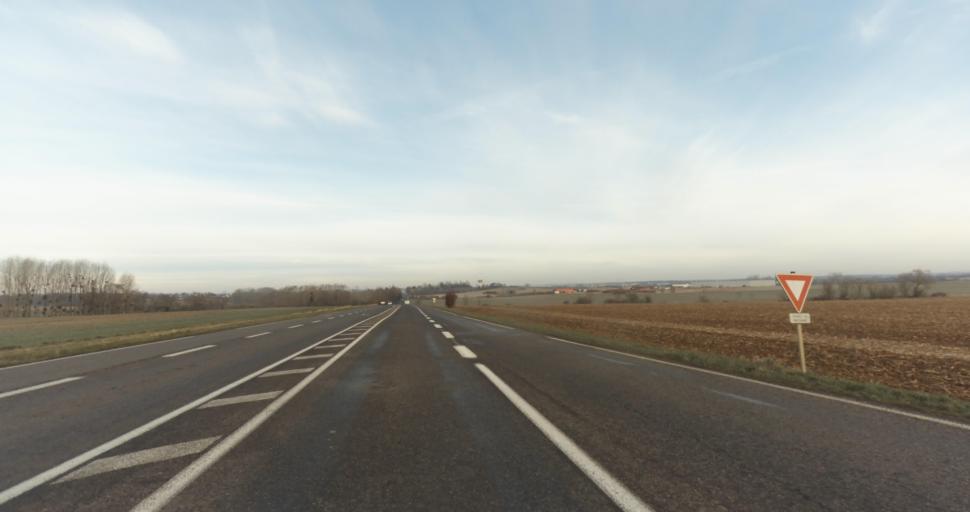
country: FR
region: Lorraine
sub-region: Departement de Meurthe-et-Moselle
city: Doncourt-les-Conflans
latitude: 49.1495
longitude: 5.9114
